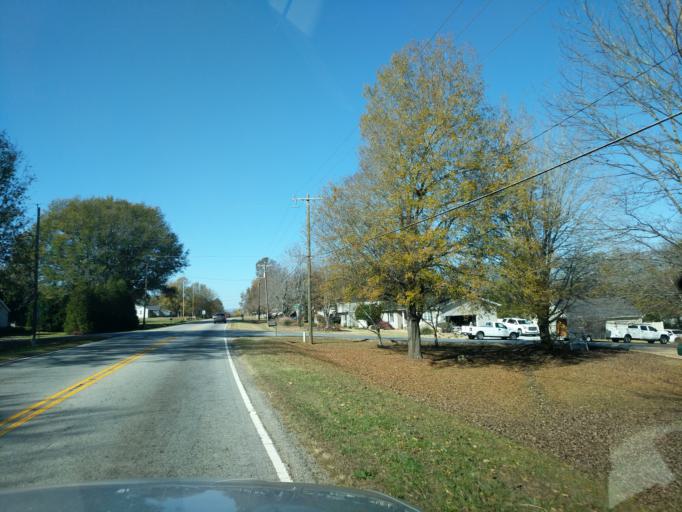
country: US
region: South Carolina
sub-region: Greenville County
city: Taylors
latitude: 34.9694
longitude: -82.3232
